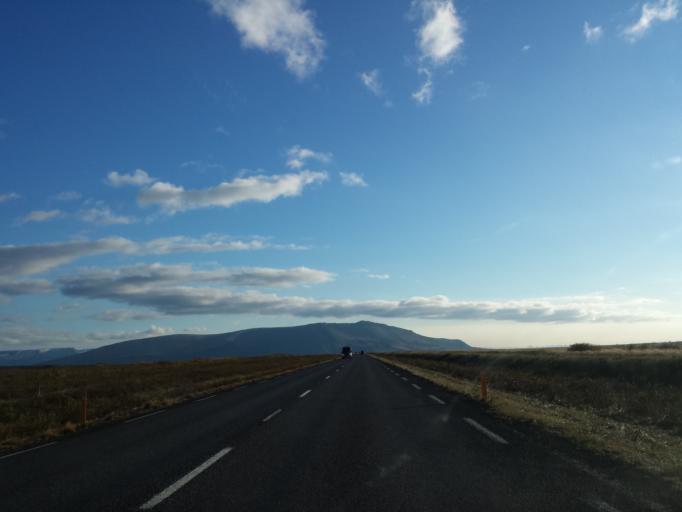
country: IS
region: West
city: Borgarnes
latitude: 64.4429
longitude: -21.9587
